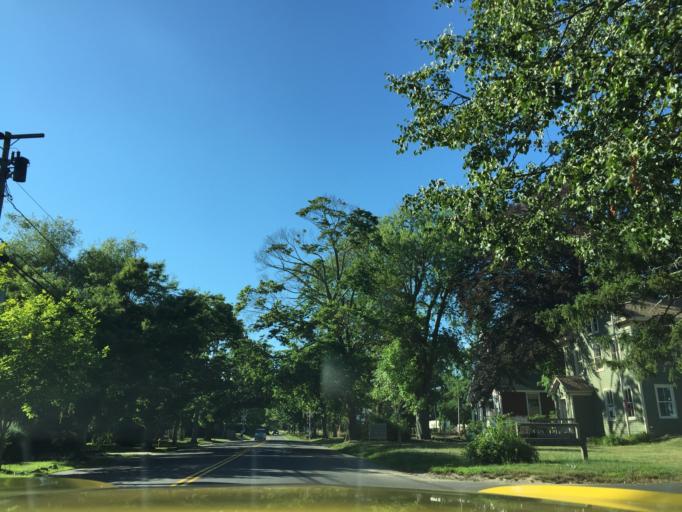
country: US
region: New York
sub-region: Suffolk County
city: Southold
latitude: 41.0631
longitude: -72.4323
